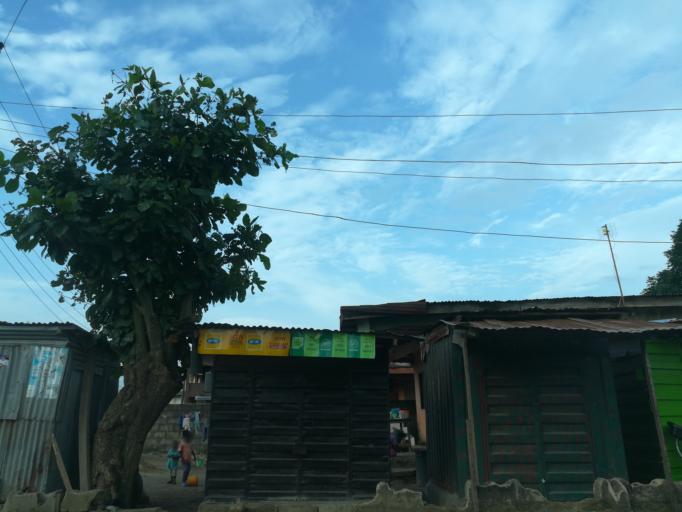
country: NG
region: Lagos
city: Ebute Ikorodu
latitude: 6.6149
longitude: 3.4739
